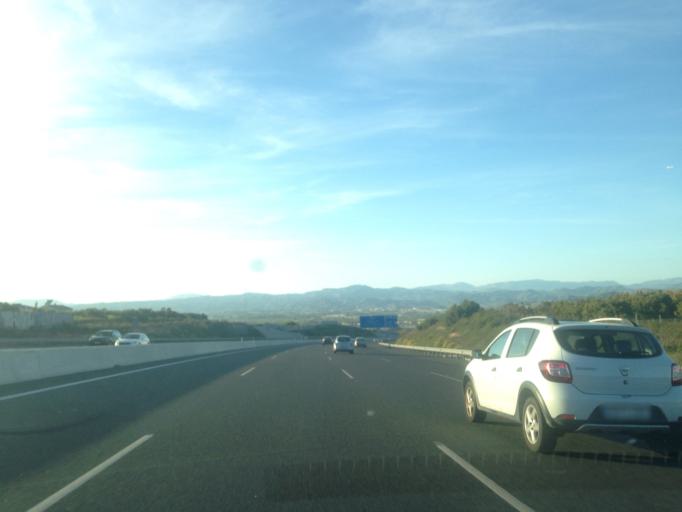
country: ES
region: Andalusia
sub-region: Provincia de Malaga
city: Alhaurin de la Torre
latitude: 36.6633
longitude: -4.5280
